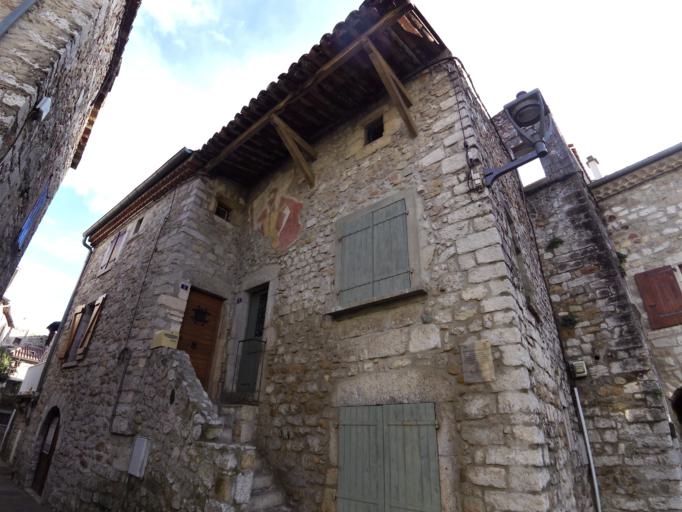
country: FR
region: Rhone-Alpes
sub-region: Departement de l'Ardeche
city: Ruoms
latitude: 44.4535
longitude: 4.3405
